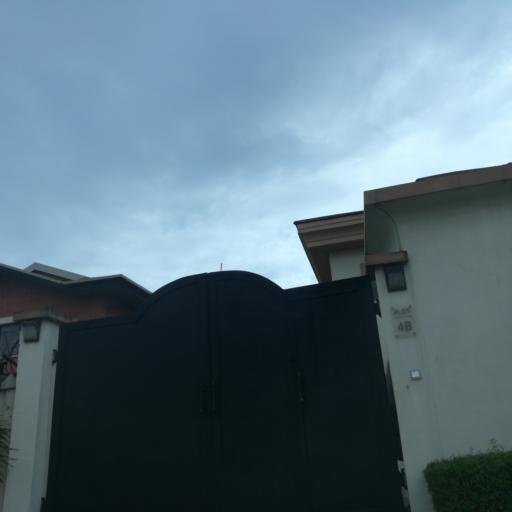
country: NG
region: Lagos
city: Ikoyi
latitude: 6.4443
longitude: 3.4675
